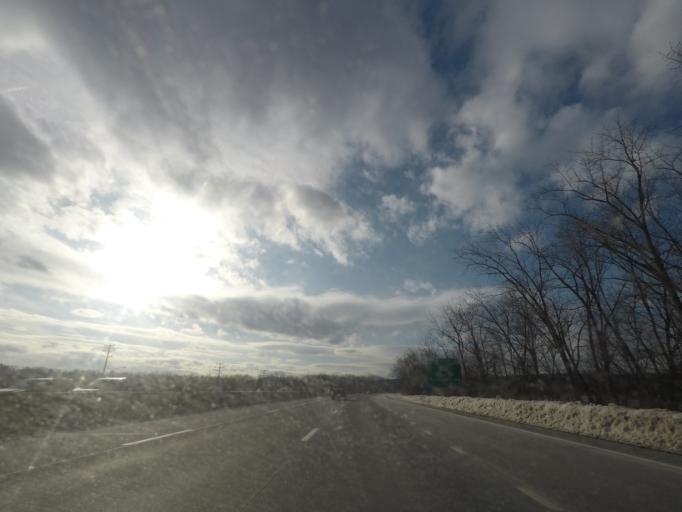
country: US
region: New York
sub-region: Schenectady County
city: Scotia
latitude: 42.8136
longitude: -73.9649
